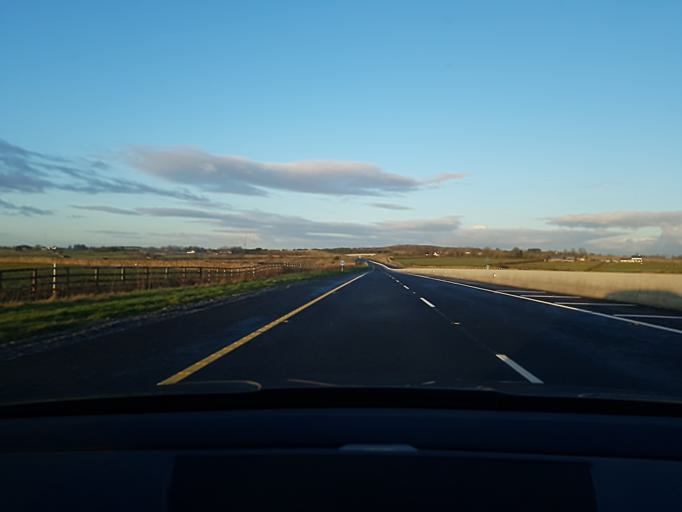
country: IE
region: Connaught
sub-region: County Galway
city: Athenry
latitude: 53.3531
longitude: -8.7968
